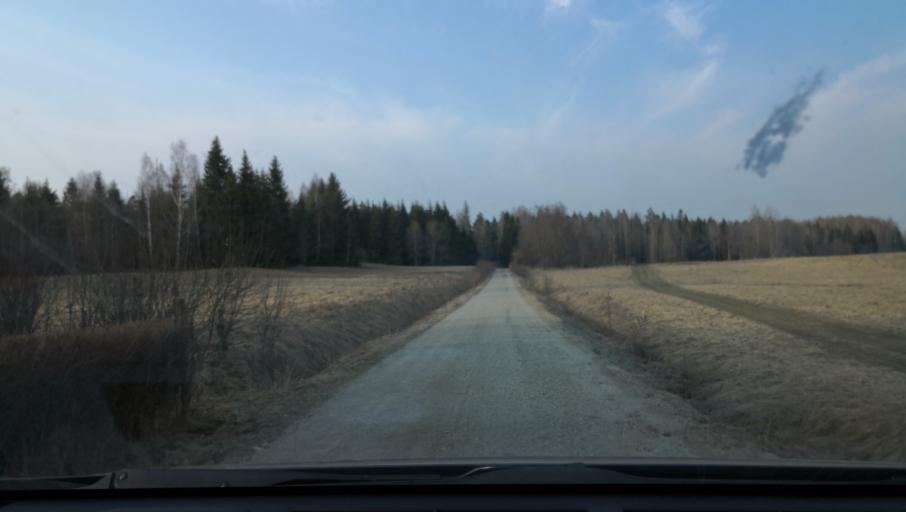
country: SE
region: OErebro
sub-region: Orebro Kommun
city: Hovsta
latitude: 59.3900
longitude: 15.2701
